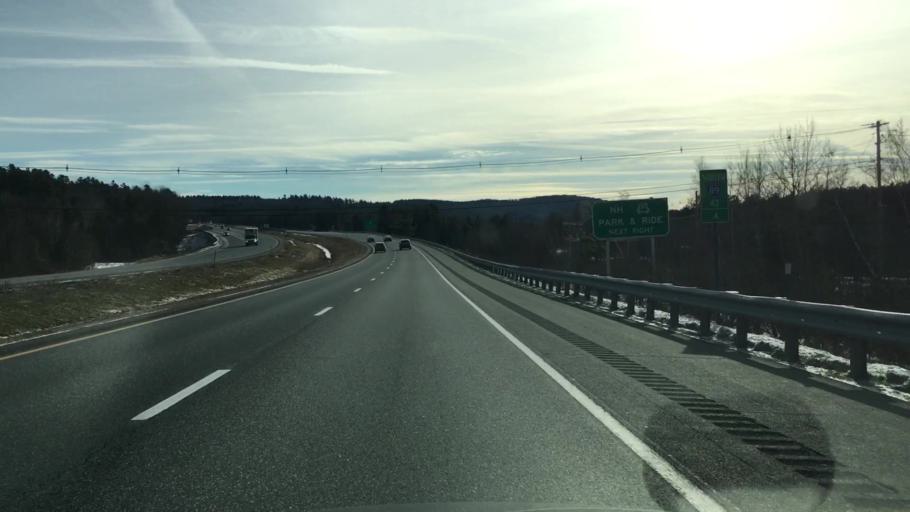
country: US
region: New Hampshire
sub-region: Sullivan County
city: Grantham
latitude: 43.5043
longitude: -72.1346
